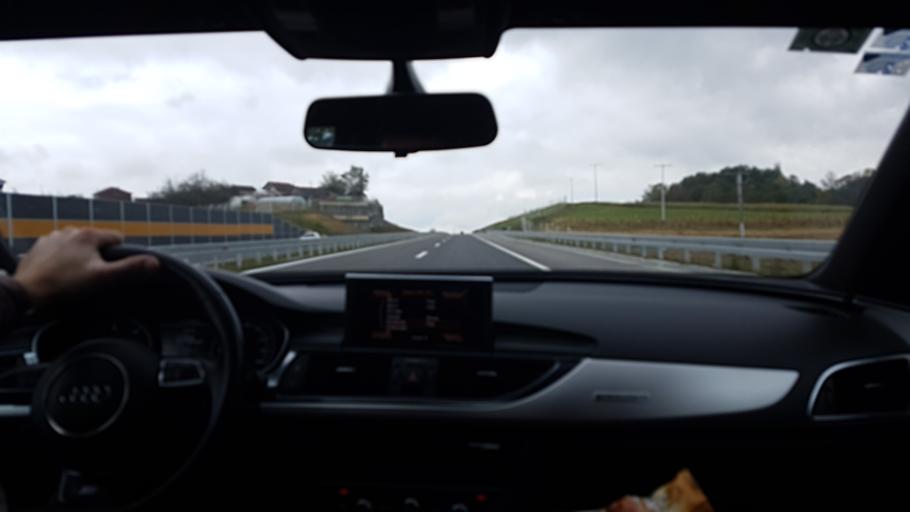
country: BA
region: Republika Srpska
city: Prnjavor
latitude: 44.8536
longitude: 17.7212
